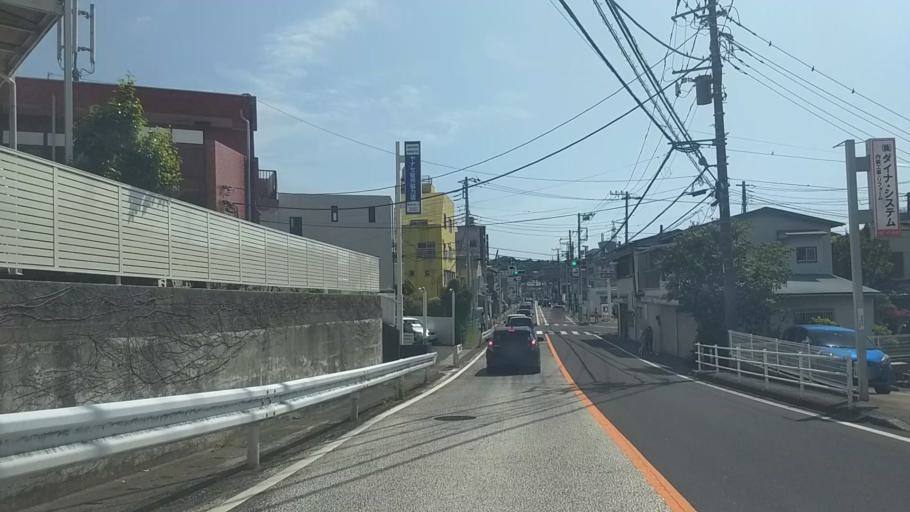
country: JP
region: Kanagawa
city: Kamakura
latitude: 35.3470
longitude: 139.5421
